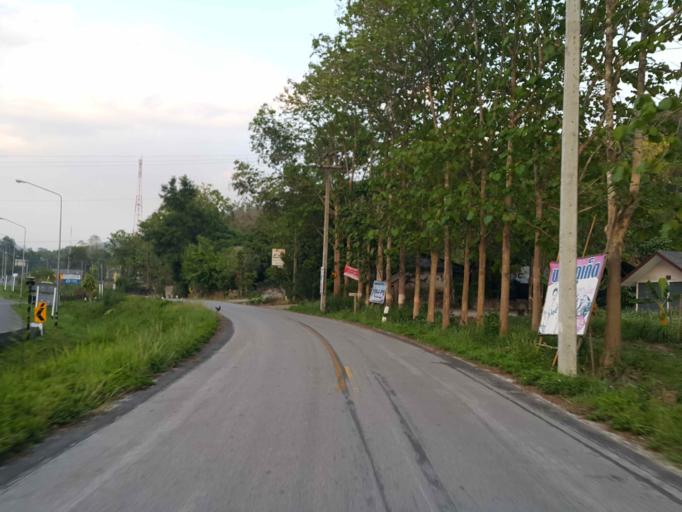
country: TH
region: Chiang Mai
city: Mae On
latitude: 19.0158
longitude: 99.3037
